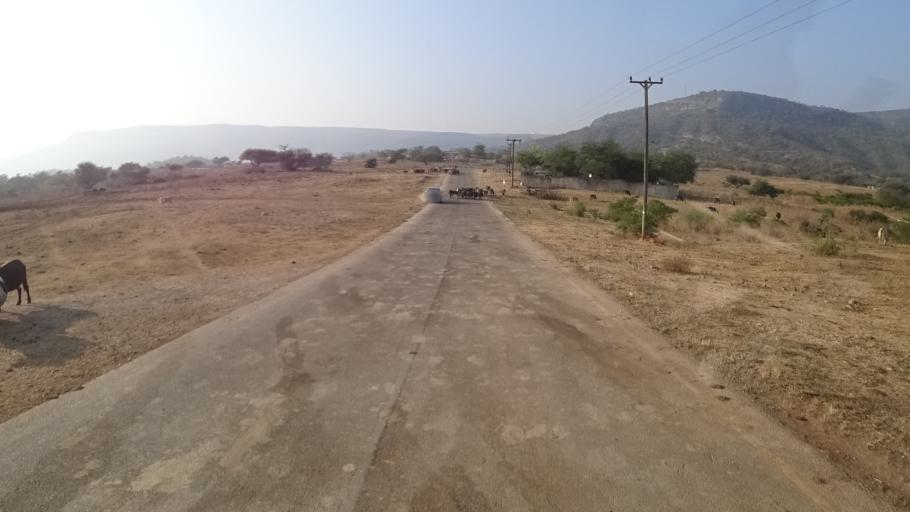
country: YE
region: Al Mahrah
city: Hawf
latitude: 16.7510
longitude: 53.3422
